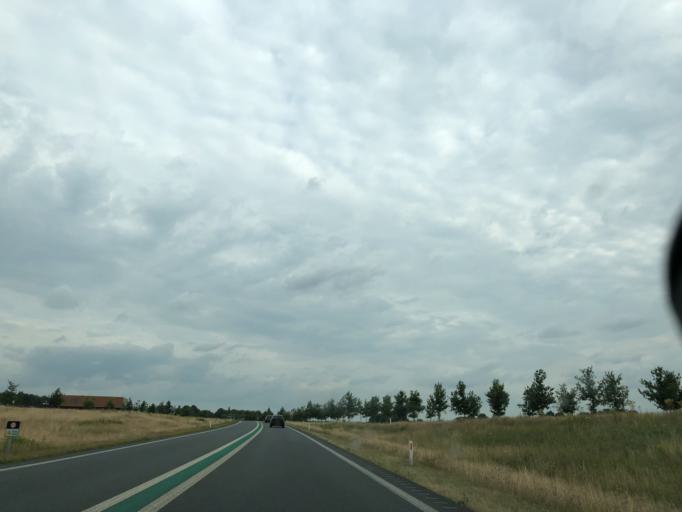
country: NL
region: Drenthe
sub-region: Gemeente Aa en Hunze
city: Anloo
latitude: 52.9977
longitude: 6.7542
